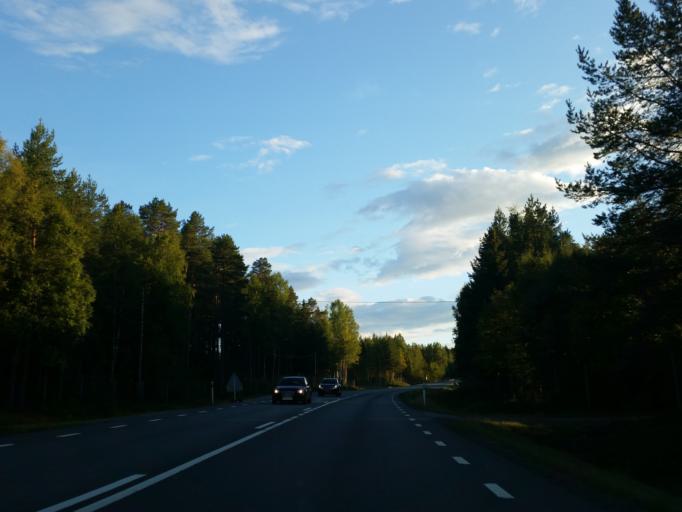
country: SE
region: Vaesterbotten
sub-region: Robertsfors Kommun
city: Robertsfors
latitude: 64.0206
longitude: 20.8378
